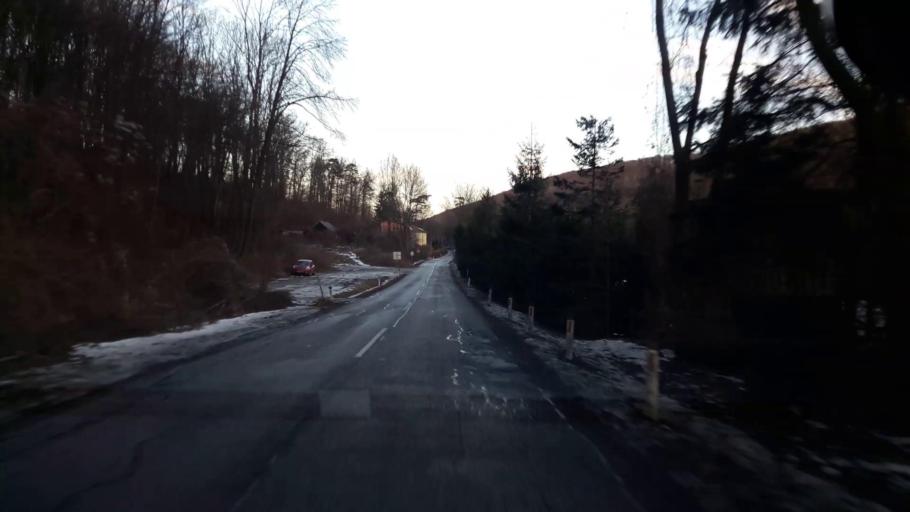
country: AT
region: Lower Austria
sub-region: Politischer Bezirk Wien-Umgebung
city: Klosterneuburg
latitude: 48.2786
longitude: 16.2787
